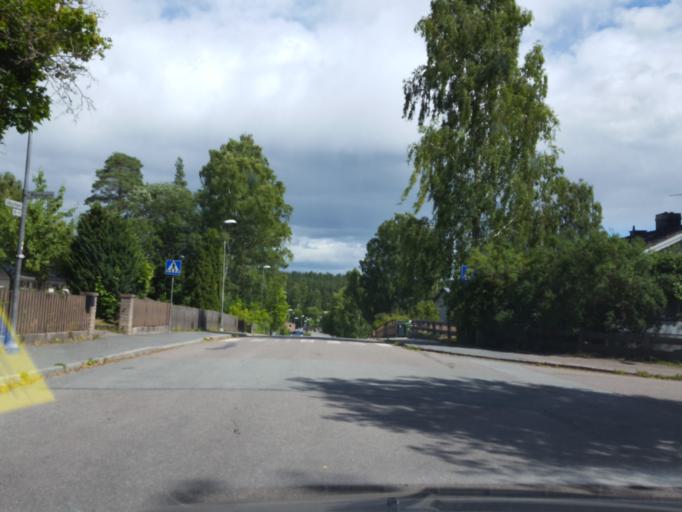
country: SE
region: Uppsala
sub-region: Uppsala Kommun
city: Saevja
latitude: 59.7968
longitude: 17.6472
